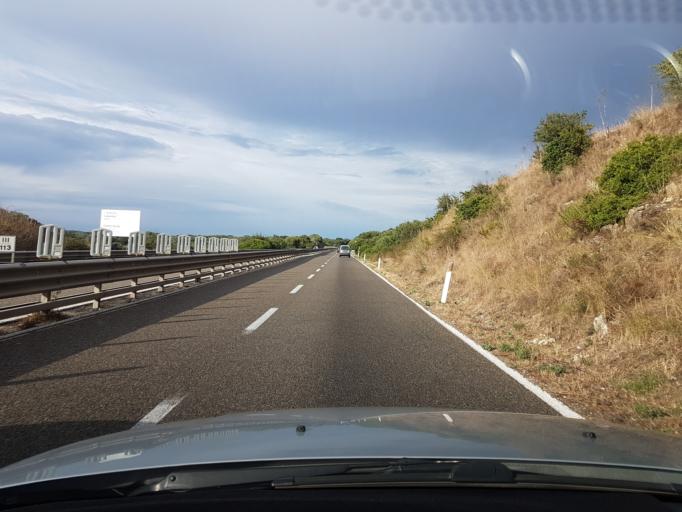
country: IT
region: Sardinia
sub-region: Provincia di Oristano
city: Bauladu
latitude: 40.0549
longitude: 8.7146
